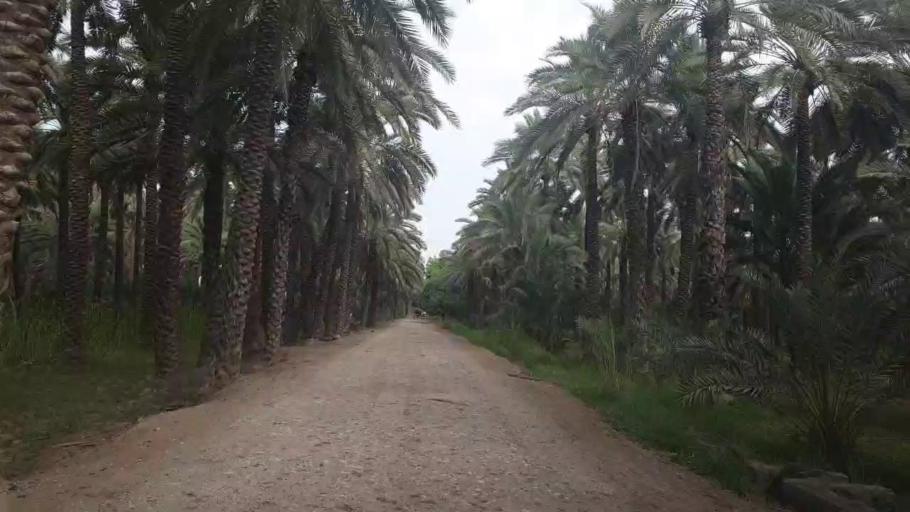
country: PK
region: Sindh
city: Sukkur
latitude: 27.6413
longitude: 68.8236
